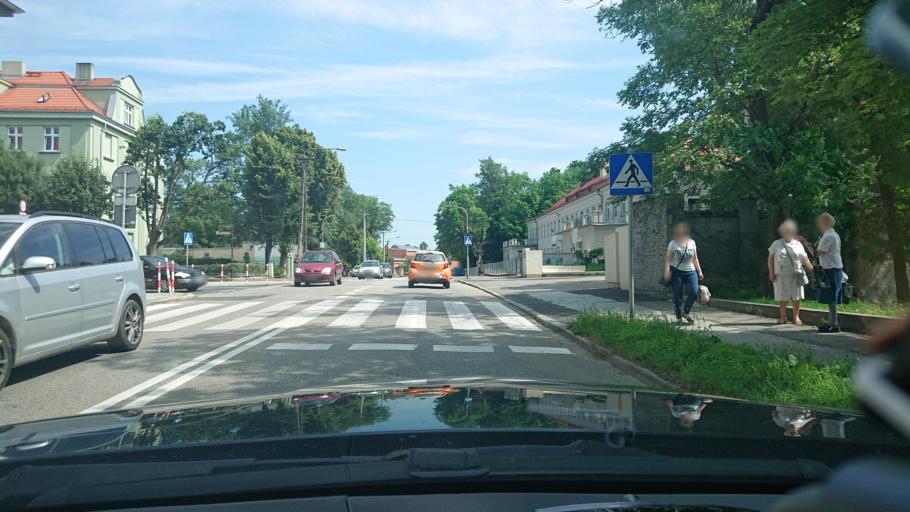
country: PL
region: Greater Poland Voivodeship
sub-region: Powiat gnieznienski
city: Gniezno
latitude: 52.5349
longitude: 17.6056
